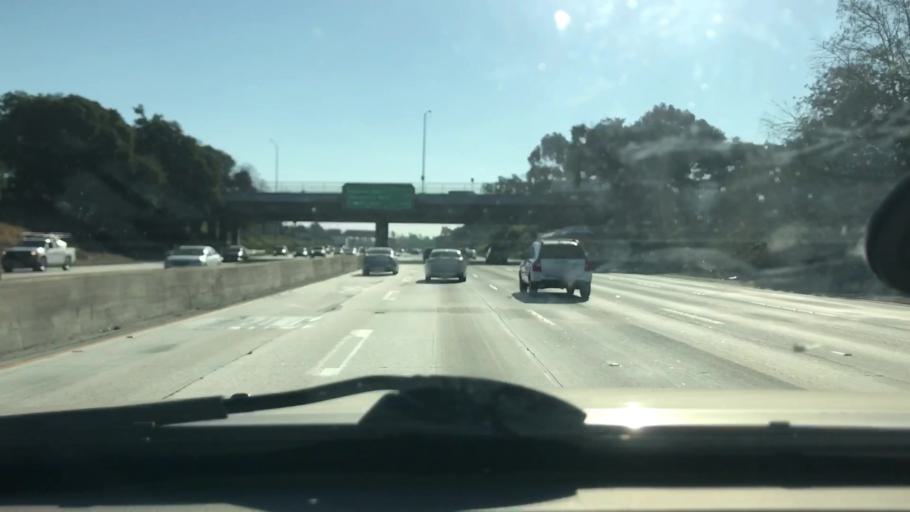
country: US
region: California
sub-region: Los Angeles County
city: Ladera Heights
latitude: 33.9723
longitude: -118.3789
